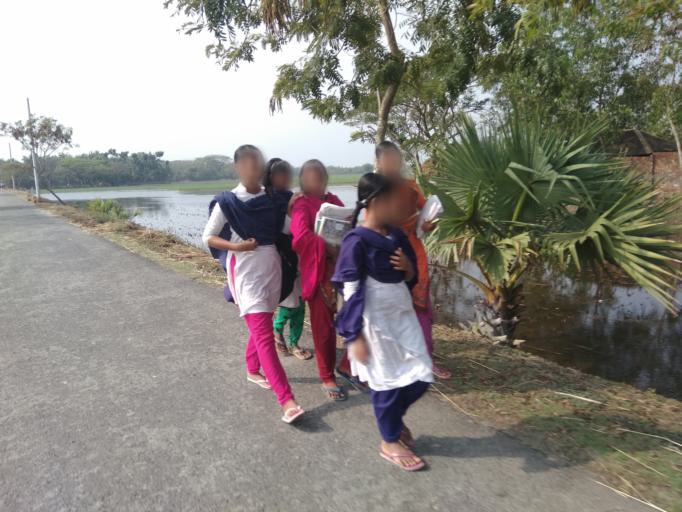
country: IN
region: West Bengal
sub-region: North 24 Parganas
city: Gosaba
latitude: 22.2592
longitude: 89.1152
